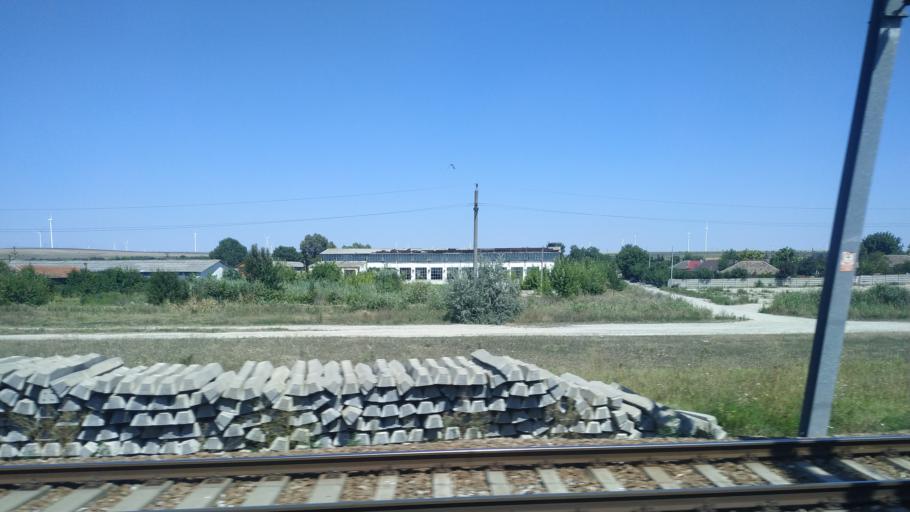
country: RO
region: Constanta
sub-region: Comuna Mircea Voda
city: Mircea Voda
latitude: 44.2670
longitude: 28.1387
